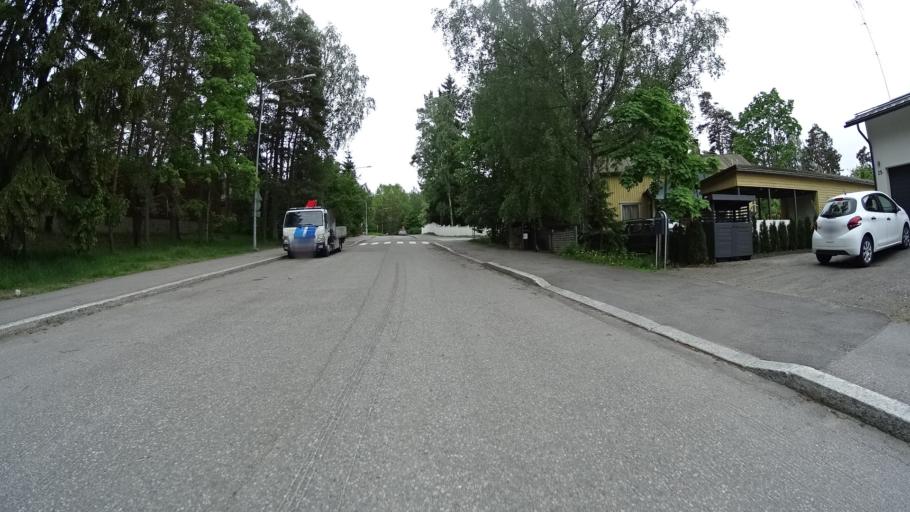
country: FI
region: Uusimaa
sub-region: Helsinki
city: Vantaa
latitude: 60.2664
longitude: 25.0646
